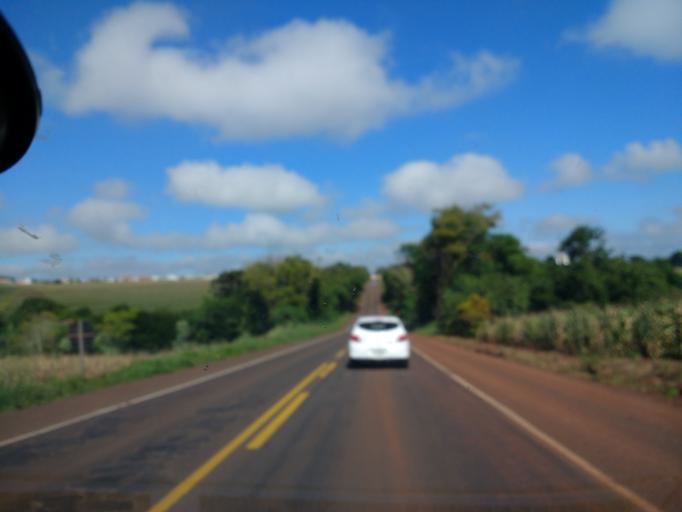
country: BR
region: Parana
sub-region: Paicandu
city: Paicandu
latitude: -23.5415
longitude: -52.2249
